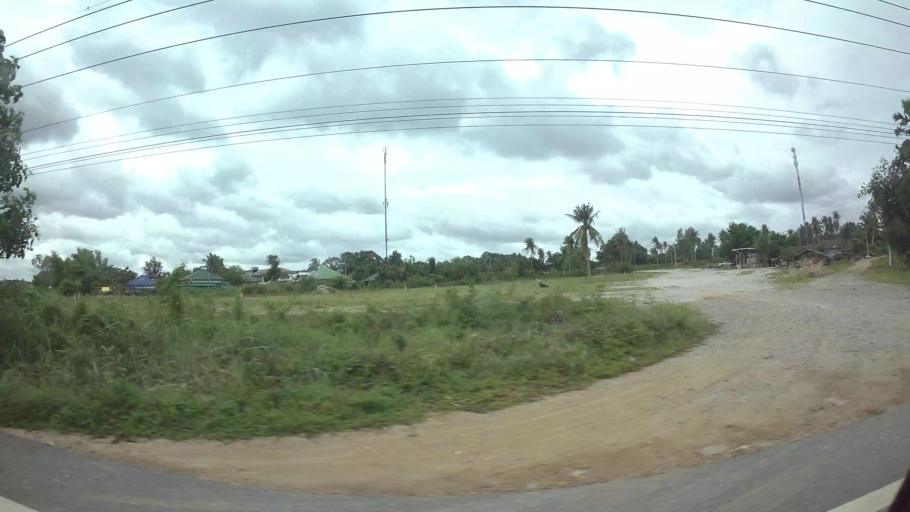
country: TH
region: Chon Buri
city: Si Racha
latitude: 13.1861
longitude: 100.9888
